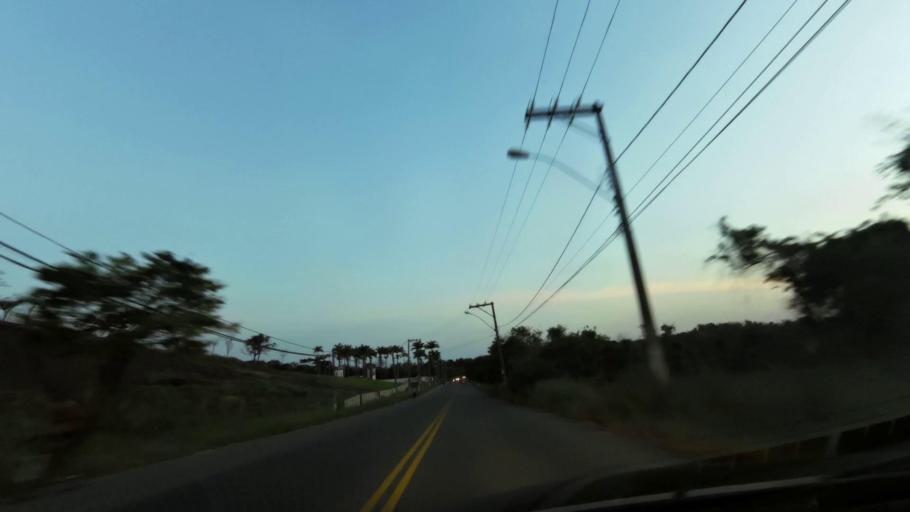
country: BR
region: Espirito Santo
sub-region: Guarapari
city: Guarapari
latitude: -20.6326
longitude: -40.4787
